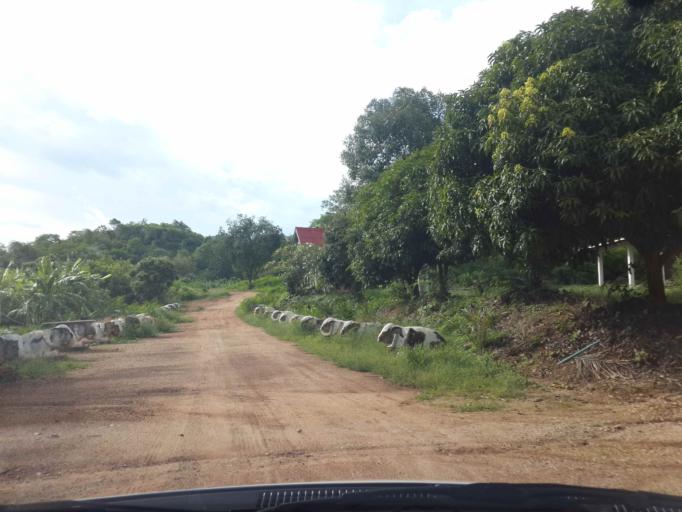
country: TH
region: Kanchanaburi
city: Dan Makham Tia
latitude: 13.7536
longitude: 99.2034
